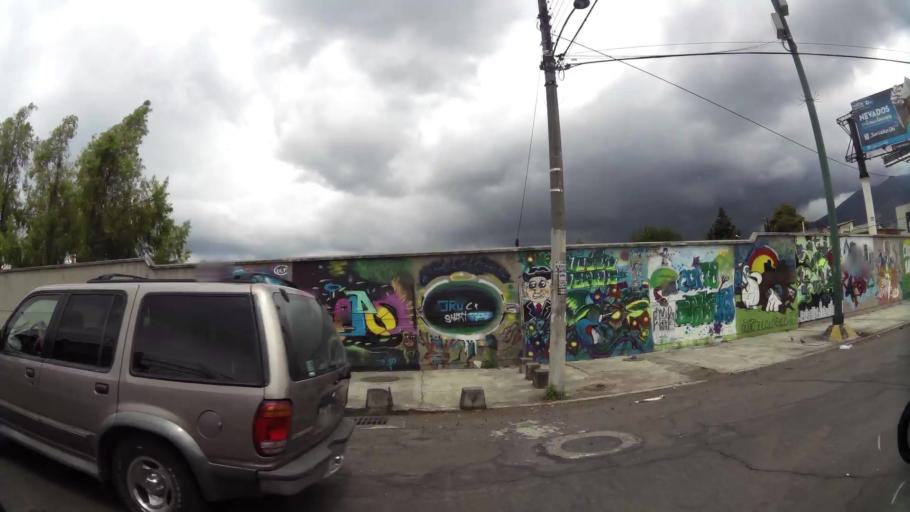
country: EC
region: Pichincha
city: Quito
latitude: -0.1675
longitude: -78.4820
